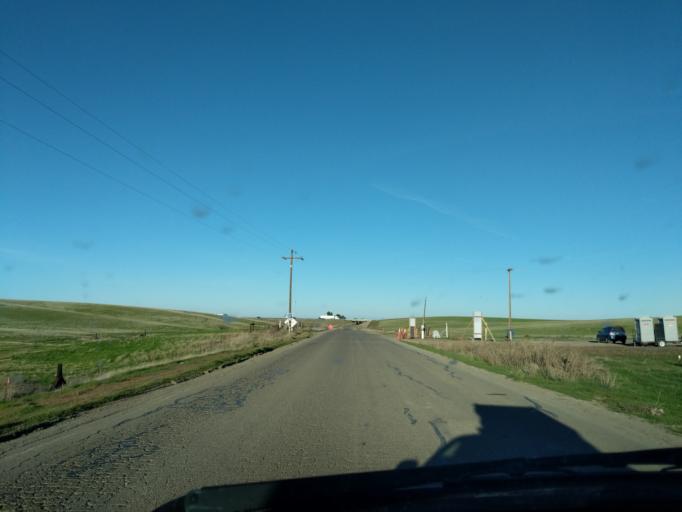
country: US
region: California
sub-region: Merced County
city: Los Banos
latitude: 37.0425
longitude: -120.9645
